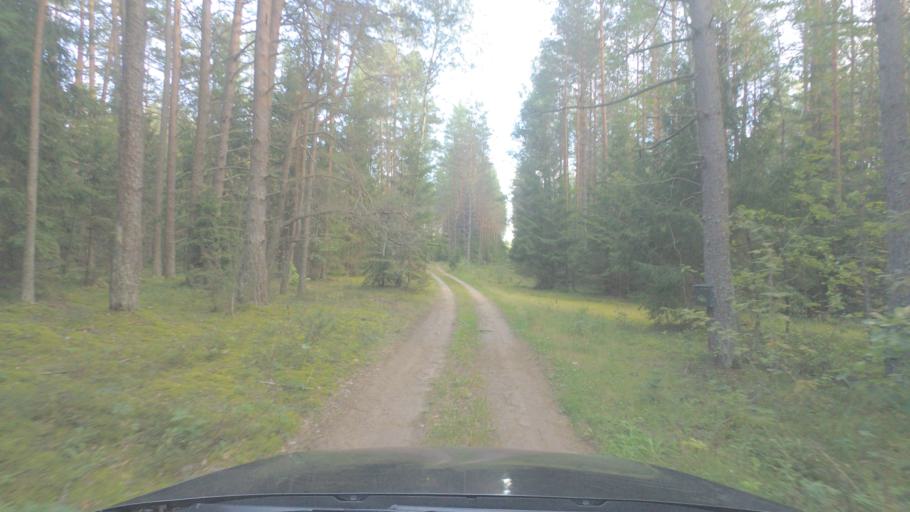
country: LT
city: Svencioneliai
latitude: 55.1610
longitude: 25.8515
